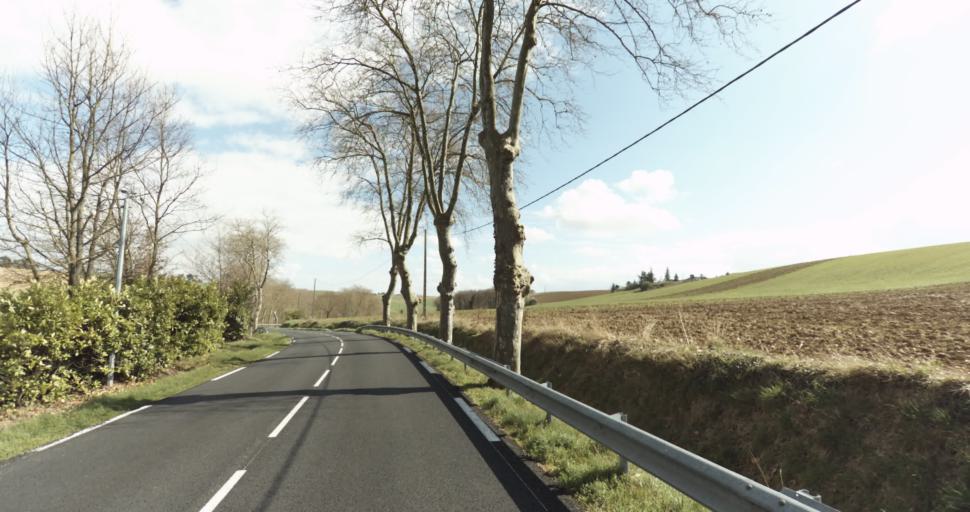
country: FR
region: Midi-Pyrenees
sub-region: Departement de la Haute-Garonne
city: Auterive
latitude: 43.3580
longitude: 1.5013
